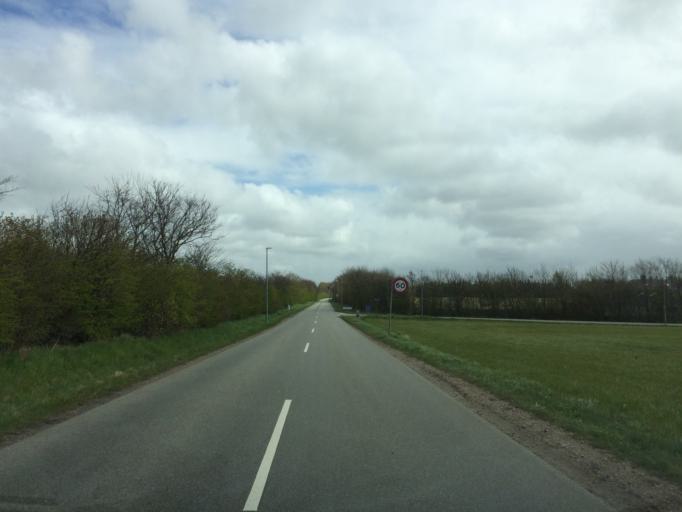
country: DK
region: South Denmark
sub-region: Varde Kommune
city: Oksbol
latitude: 55.5395
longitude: 8.3440
